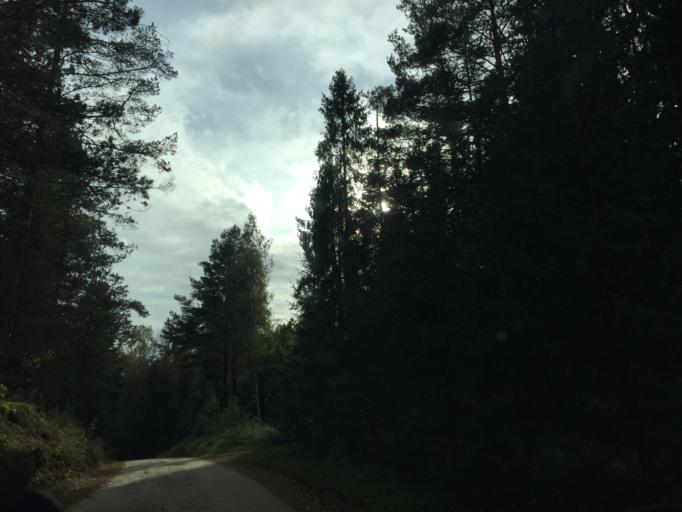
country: LV
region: Jaunpils
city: Jaunpils
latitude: 56.5735
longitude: 23.0244
